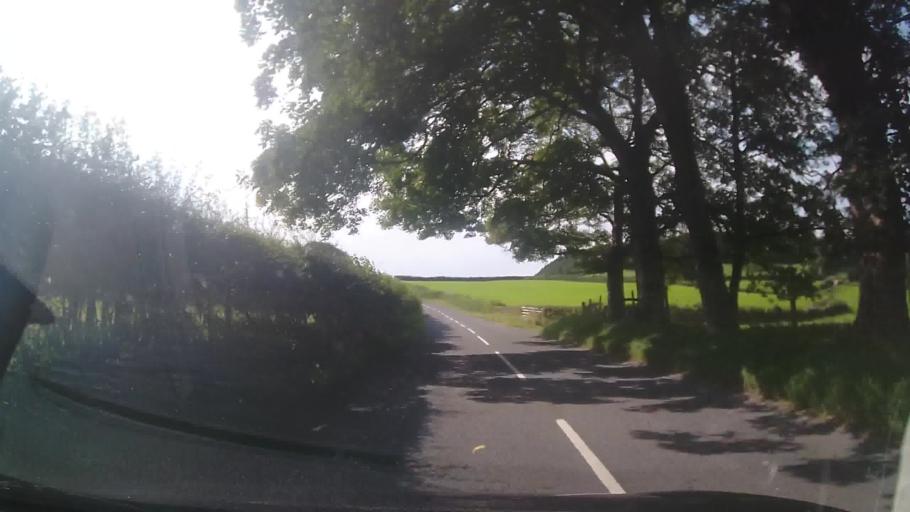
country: GB
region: Wales
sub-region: Sir Powys
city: Rhayader
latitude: 52.2979
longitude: -3.5195
